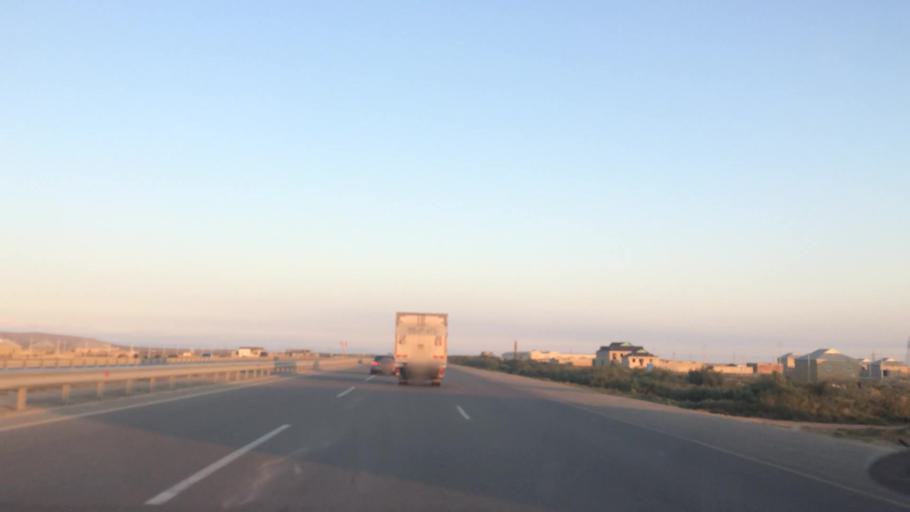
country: AZ
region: Baki
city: Qobustan
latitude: 39.9686
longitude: 49.2697
